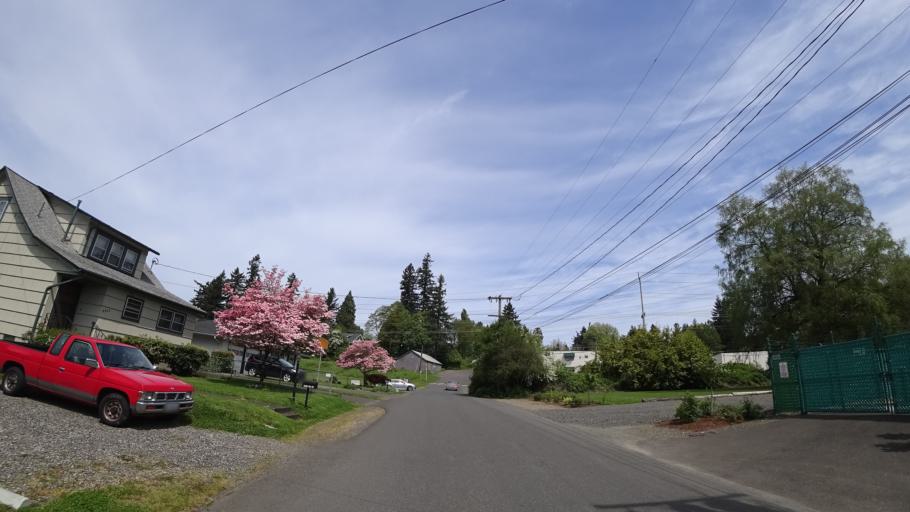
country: US
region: Oregon
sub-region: Clackamas County
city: Milwaukie
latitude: 45.4579
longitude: -122.6074
